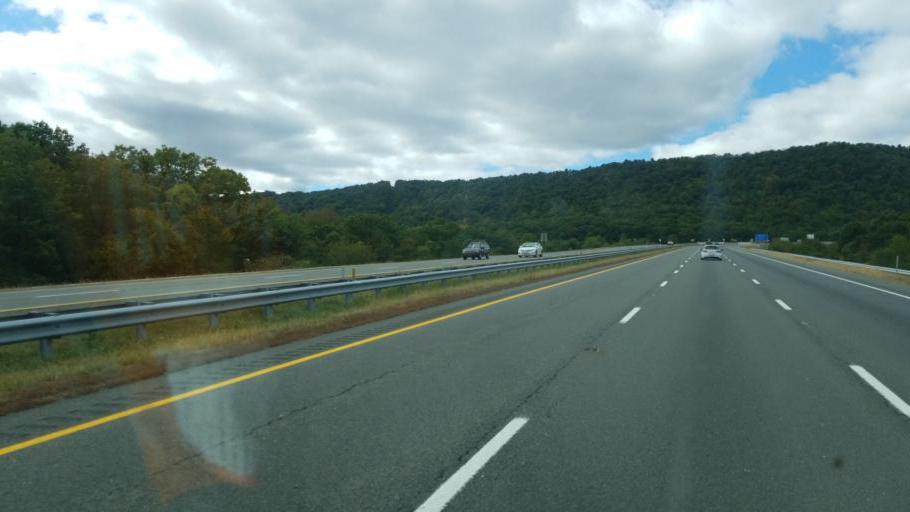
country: US
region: Maryland
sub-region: Washington County
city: Hancock
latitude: 39.7095
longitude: -78.2707
